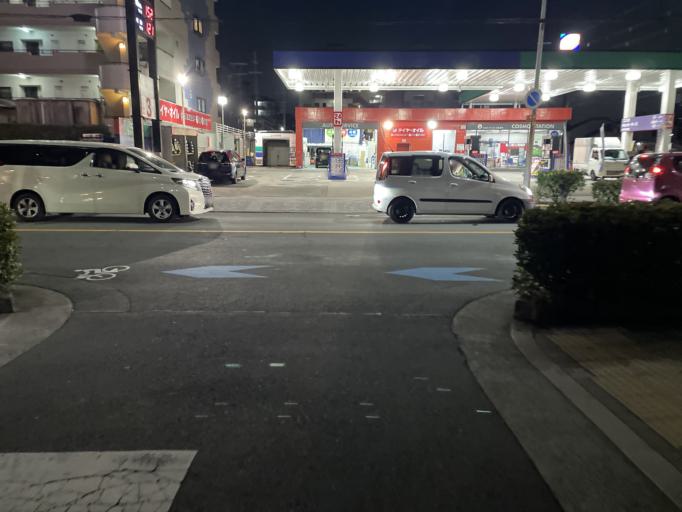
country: JP
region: Osaka
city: Ibaraki
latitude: 34.8000
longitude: 135.5786
